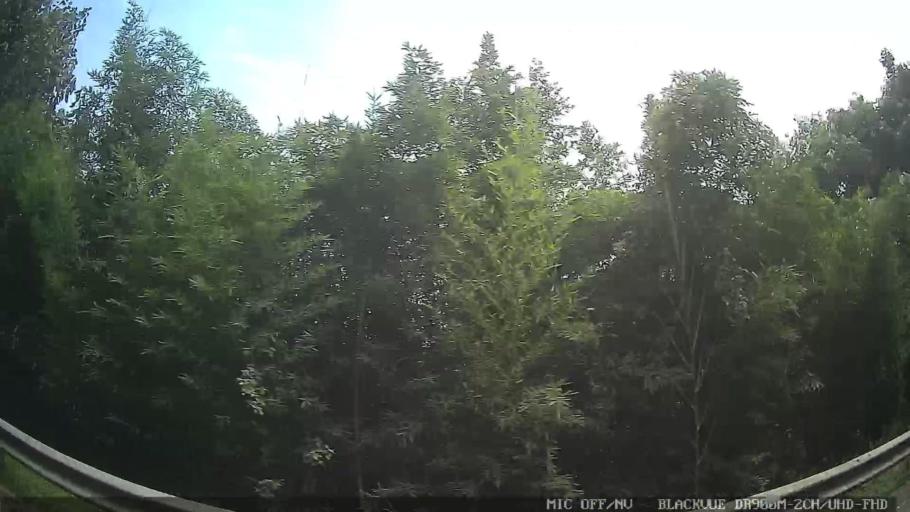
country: BR
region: Sao Paulo
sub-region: Ribeirao Pires
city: Ribeirao Pires
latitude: -23.6880
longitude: -46.3867
